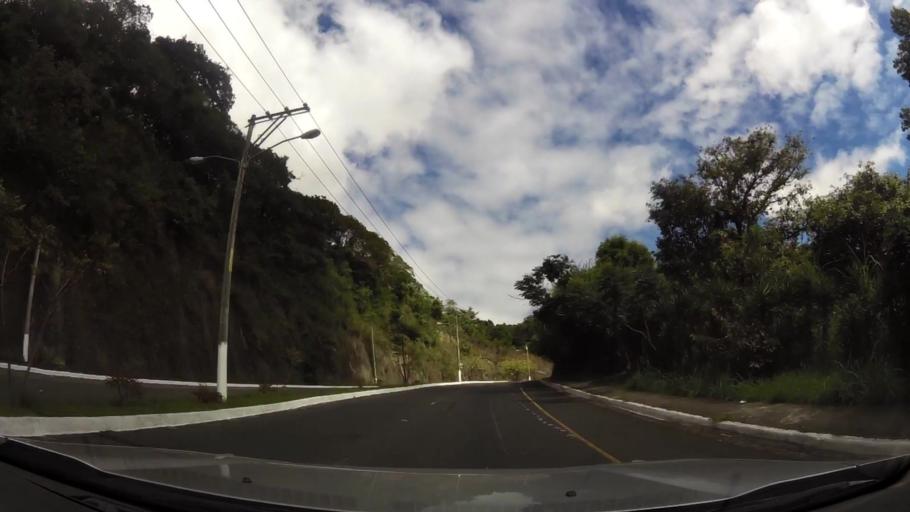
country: GT
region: Guatemala
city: Guatemala City
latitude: 14.6494
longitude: -90.5576
